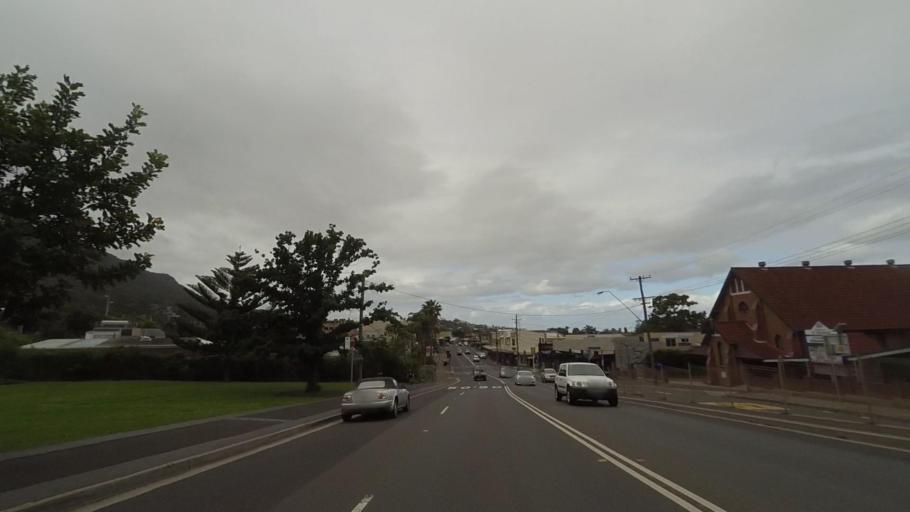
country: AU
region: New South Wales
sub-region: Wollongong
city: Bulli
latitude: -34.3162
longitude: 150.9211
